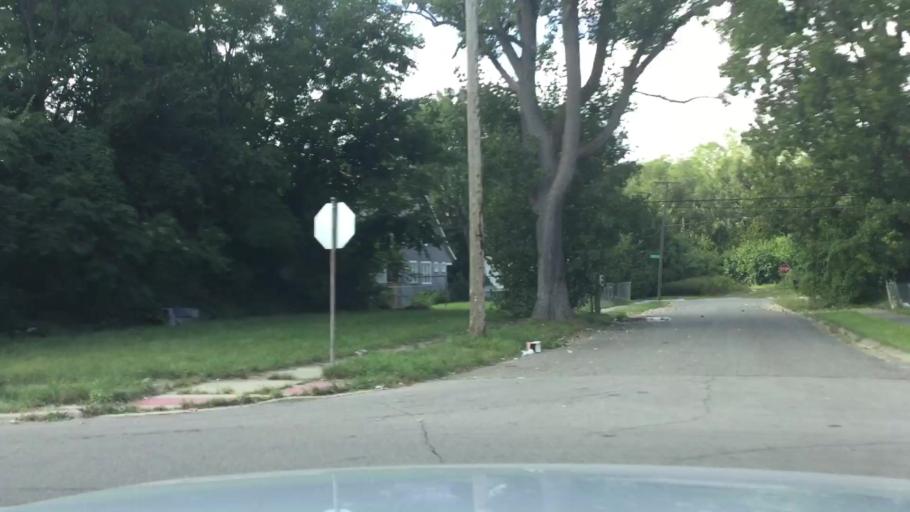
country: US
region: Michigan
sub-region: Wayne County
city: Dearborn
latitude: 42.3570
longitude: -83.1462
